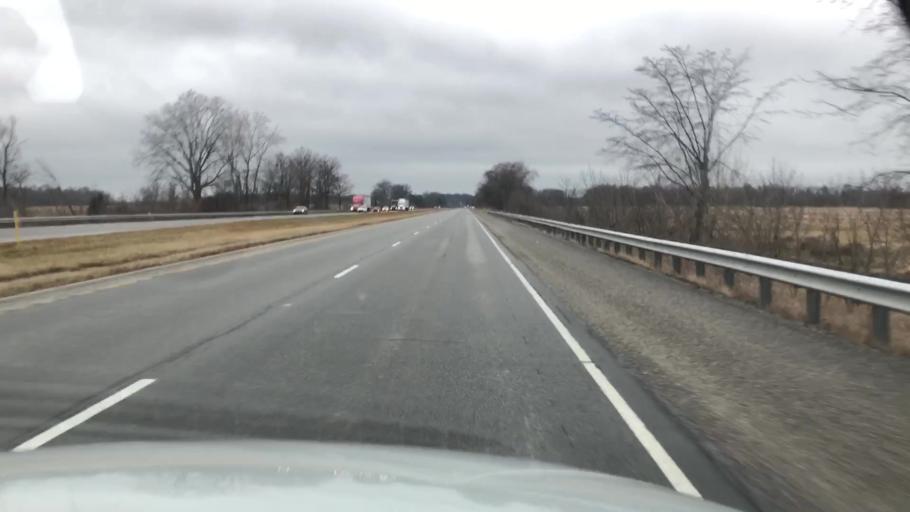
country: US
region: Indiana
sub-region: Whitley County
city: Churubusco
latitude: 41.1260
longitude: -85.3152
